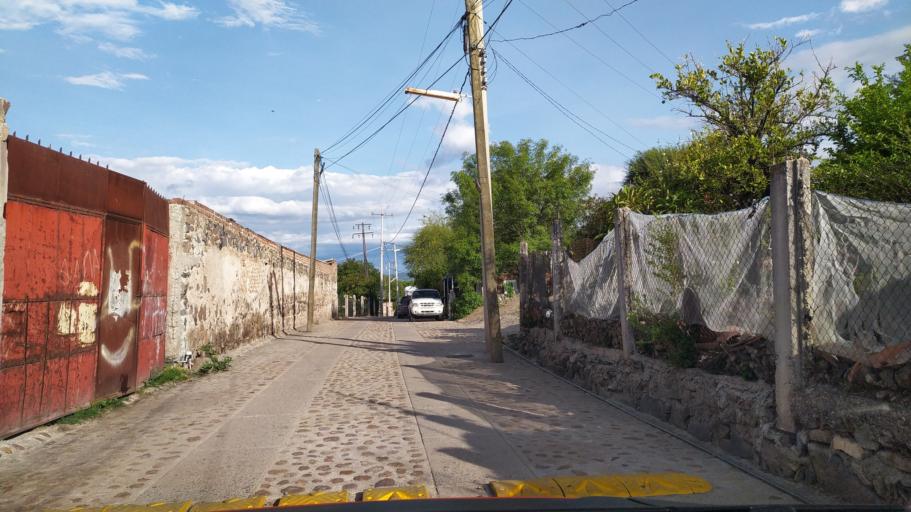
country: MX
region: Guanajuato
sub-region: San Francisco del Rincon
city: San Ignacio de Hidalgo
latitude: 20.9275
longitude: -101.9189
